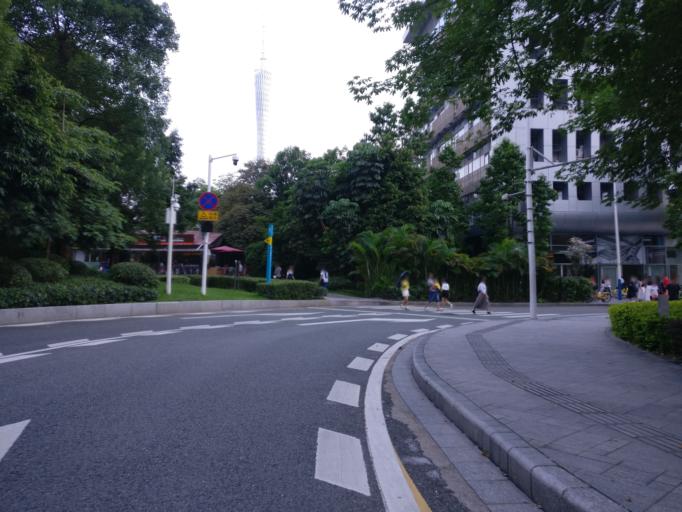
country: CN
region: Guangdong
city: Wushan
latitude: 23.1198
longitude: 113.3184
